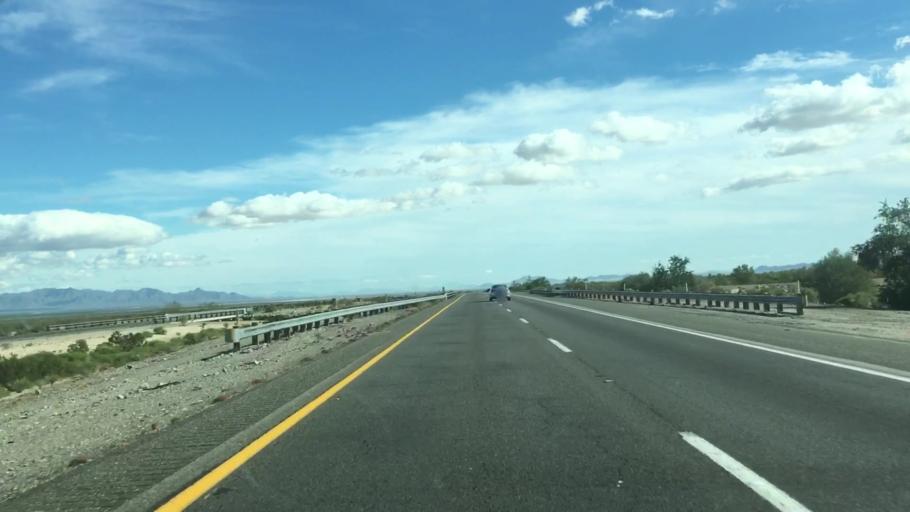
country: US
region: California
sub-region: Riverside County
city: Mesa Verde
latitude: 33.6626
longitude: -115.1772
